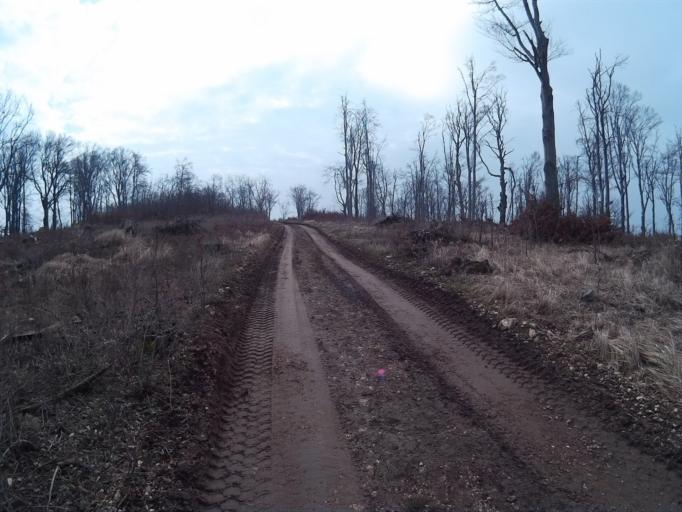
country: HU
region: Veszprem
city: Zirc
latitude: 47.1883
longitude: 17.8317
